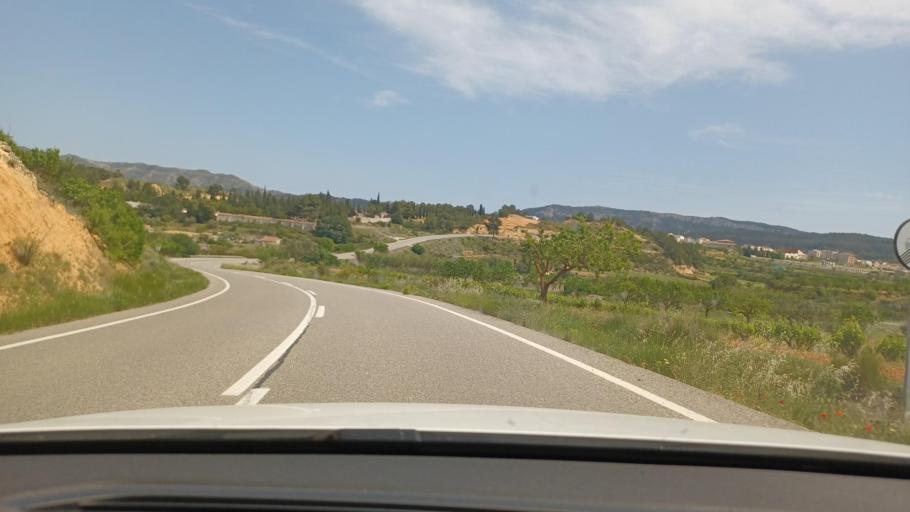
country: ES
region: Catalonia
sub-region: Provincia de Tarragona
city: Gandesa
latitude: 41.0642
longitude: 0.4333
